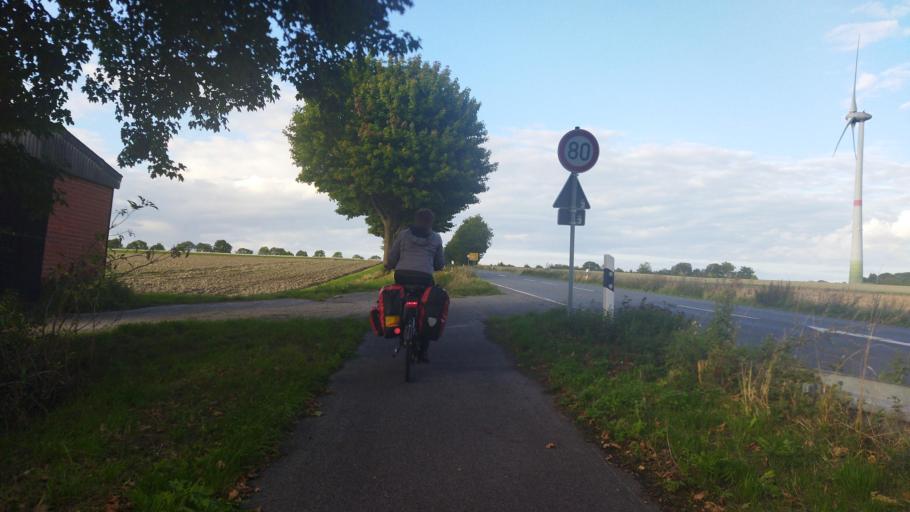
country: DE
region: North Rhine-Westphalia
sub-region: Regierungsbezirk Munster
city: Billerbeck
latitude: 51.9495
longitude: 7.2640
